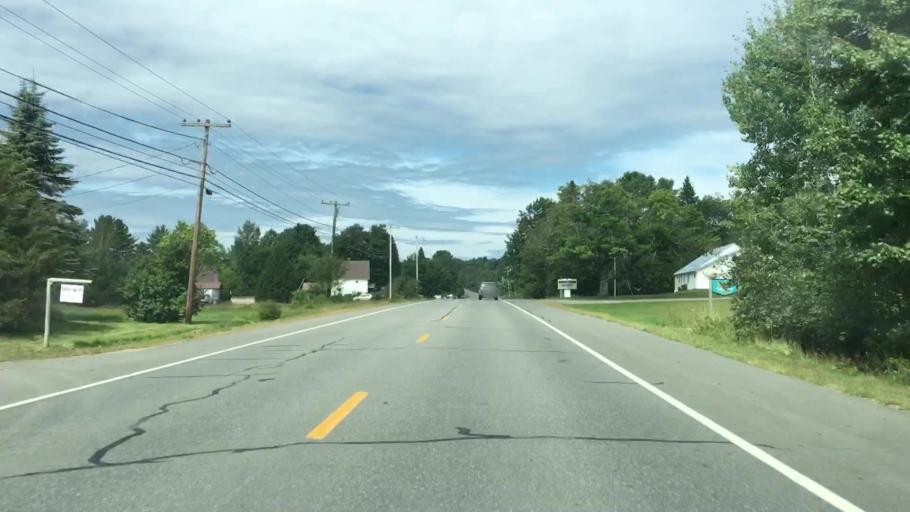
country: US
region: Maine
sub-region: Piscataquis County
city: Milo
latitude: 45.2716
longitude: -68.9993
